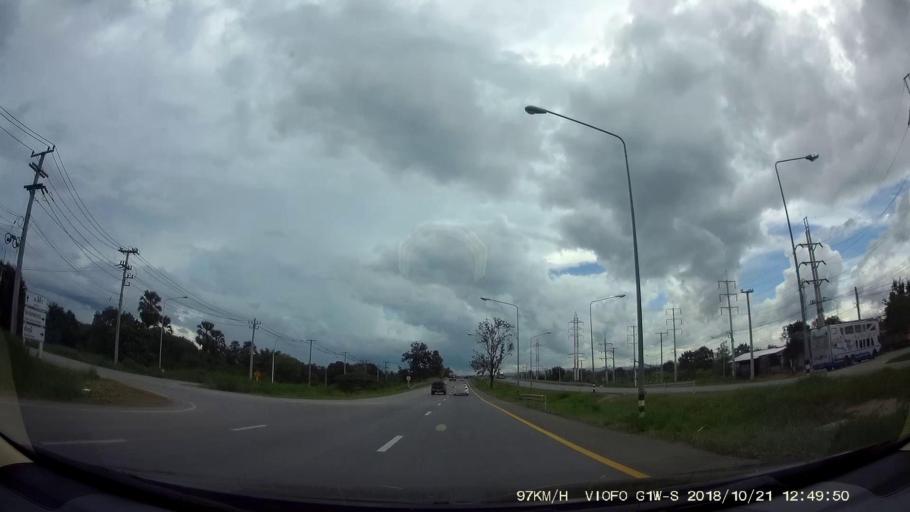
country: TH
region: Nakhon Ratchasima
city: Amphoe Sikhiu
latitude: 14.8908
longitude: 101.6865
